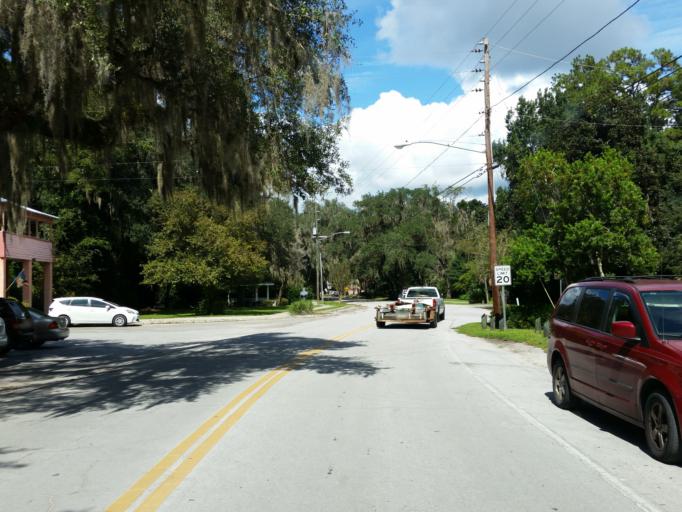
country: US
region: Florida
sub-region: Alachua County
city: Gainesville
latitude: 29.5050
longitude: -82.2796
